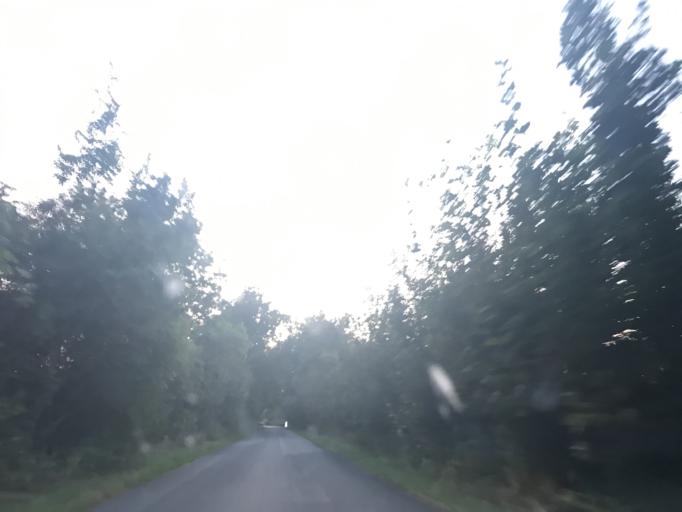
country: DE
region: Berlin
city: Gatow
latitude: 52.4817
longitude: 13.1691
